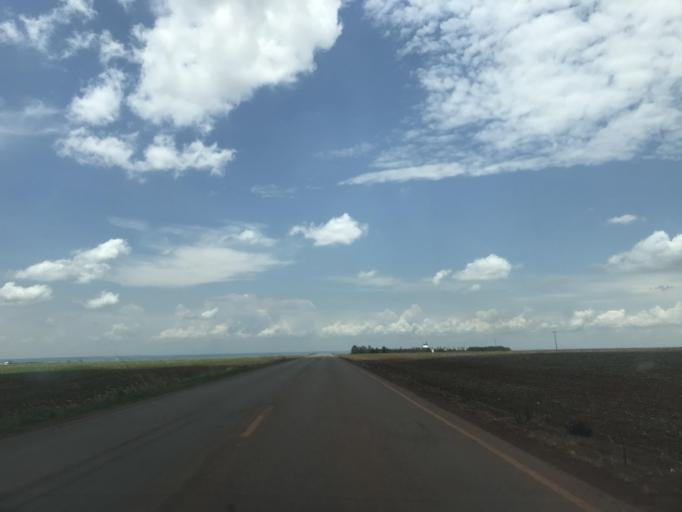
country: BR
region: Goias
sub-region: Vianopolis
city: Vianopolis
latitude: -16.5369
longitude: -48.2535
